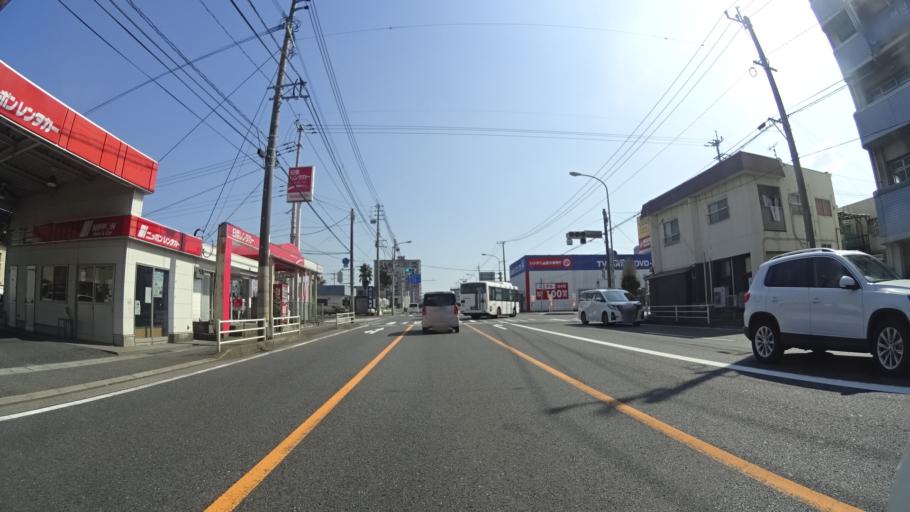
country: JP
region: Fukuoka
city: Kanda
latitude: 33.7851
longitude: 130.9822
